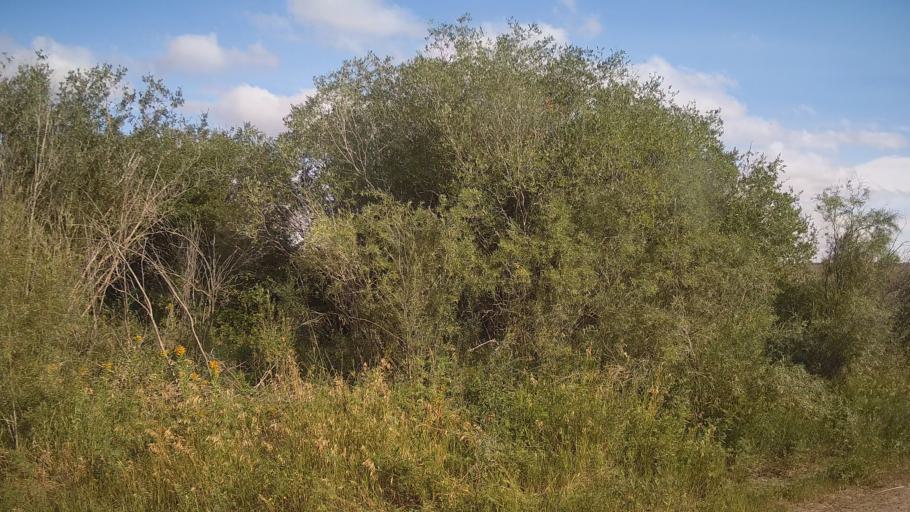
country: CA
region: Alberta
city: Brooks
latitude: 50.9176
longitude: -111.8989
